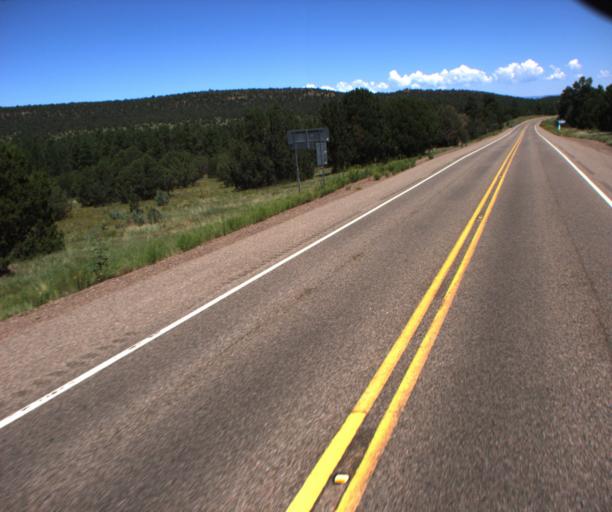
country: US
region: Arizona
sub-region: Gila County
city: San Carlos
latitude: 33.6755
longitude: -110.5728
